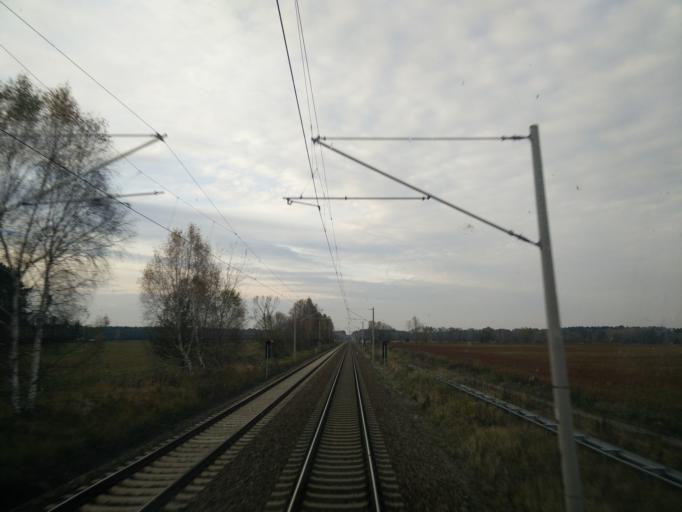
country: DE
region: Brandenburg
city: Halbe
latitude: 52.1292
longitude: 13.6800
